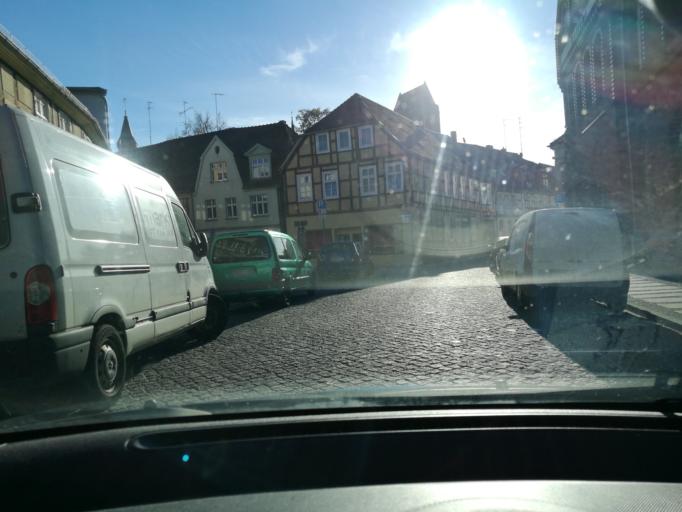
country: DE
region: Brandenburg
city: Perleberg
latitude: 53.0785
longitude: 11.8621
